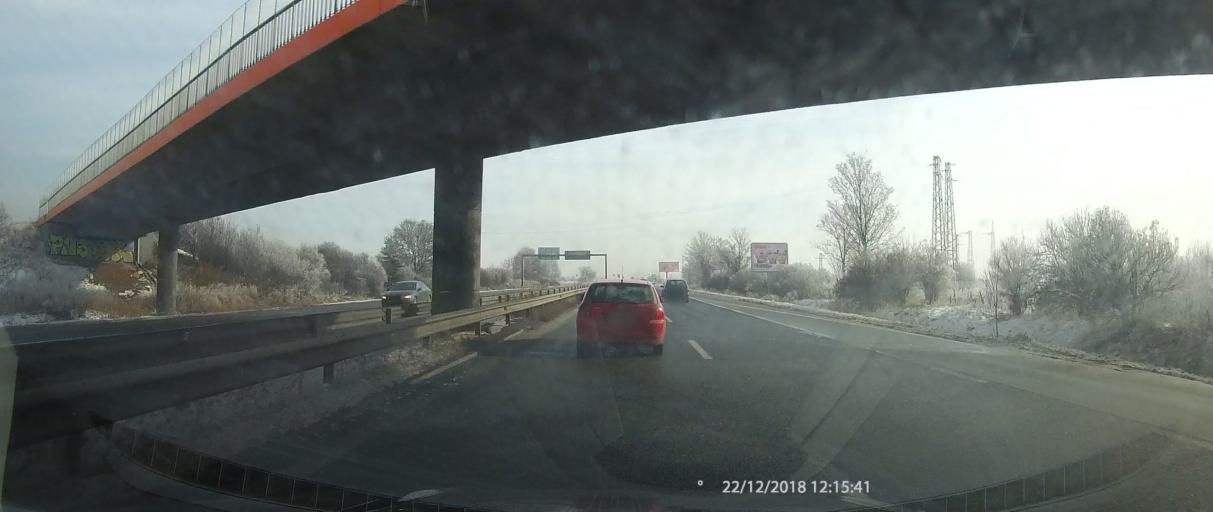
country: BG
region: Sofia-Capital
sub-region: Stolichna Obshtina
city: Bukhovo
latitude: 42.7237
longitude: 23.5479
